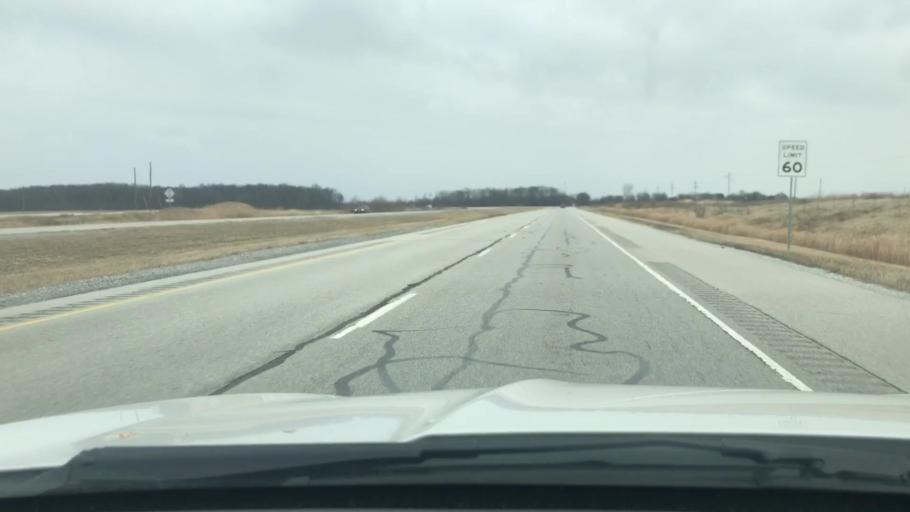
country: US
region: Indiana
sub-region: Carroll County
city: Delphi
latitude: 40.6336
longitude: -86.5903
